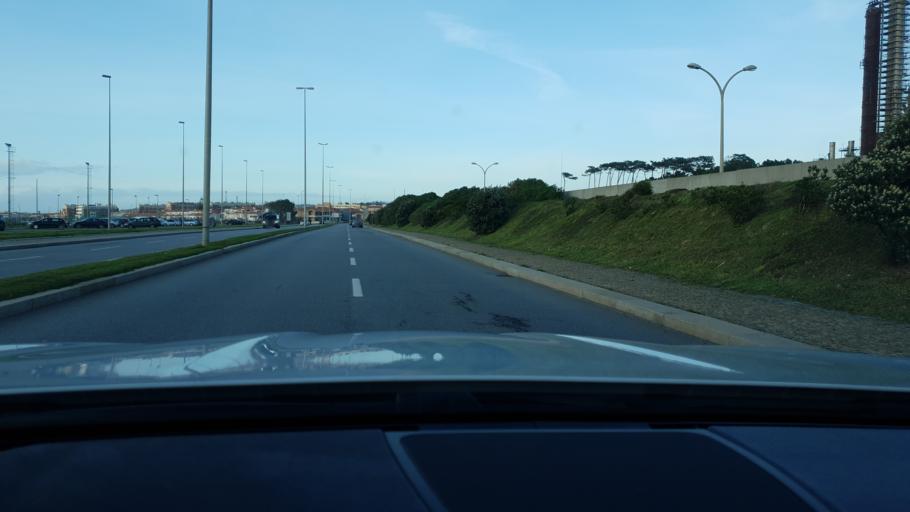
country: PT
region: Porto
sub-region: Matosinhos
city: Leca da Palmeira
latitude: 41.2169
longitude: -8.7128
